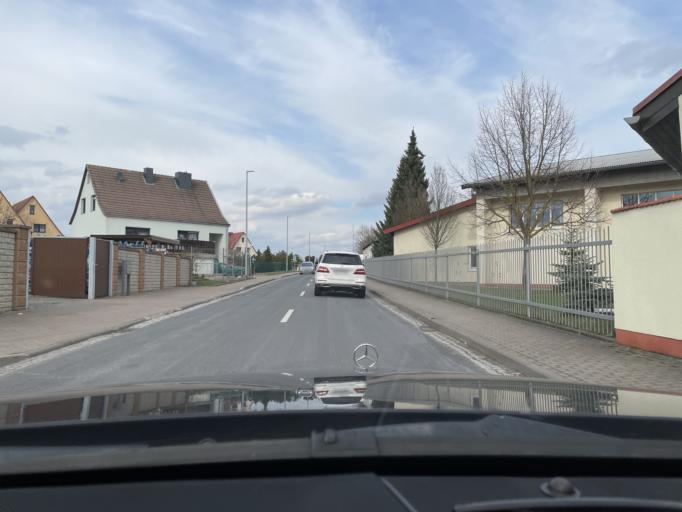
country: DE
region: Thuringia
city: Deuna
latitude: 51.3271
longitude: 10.4440
